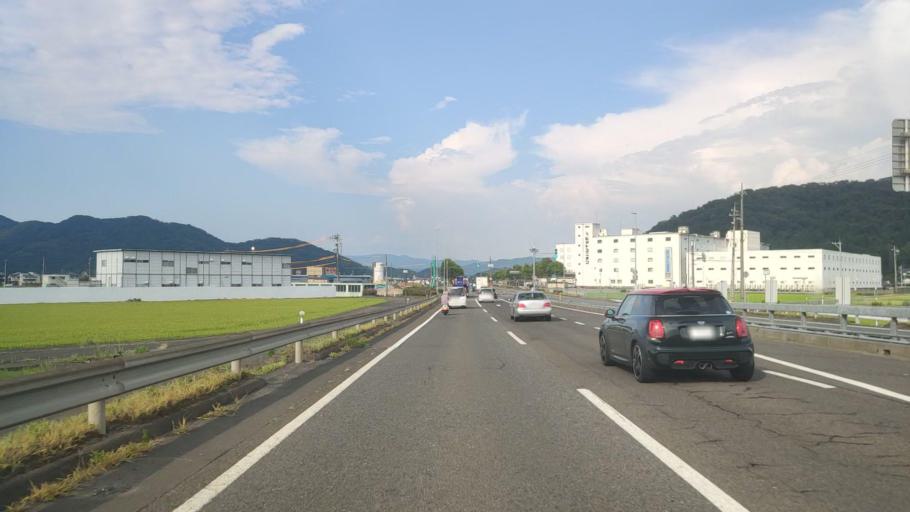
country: JP
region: Fukui
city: Takefu
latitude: 35.8794
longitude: 136.1718
